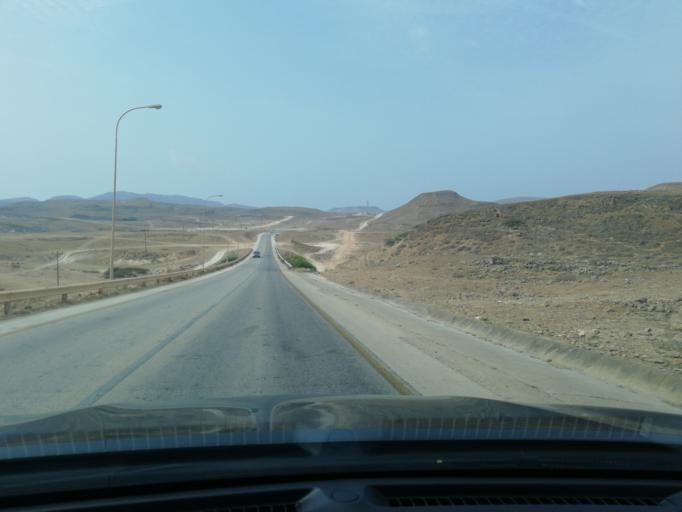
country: OM
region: Zufar
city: Salalah
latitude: 16.9235
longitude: 53.8426
